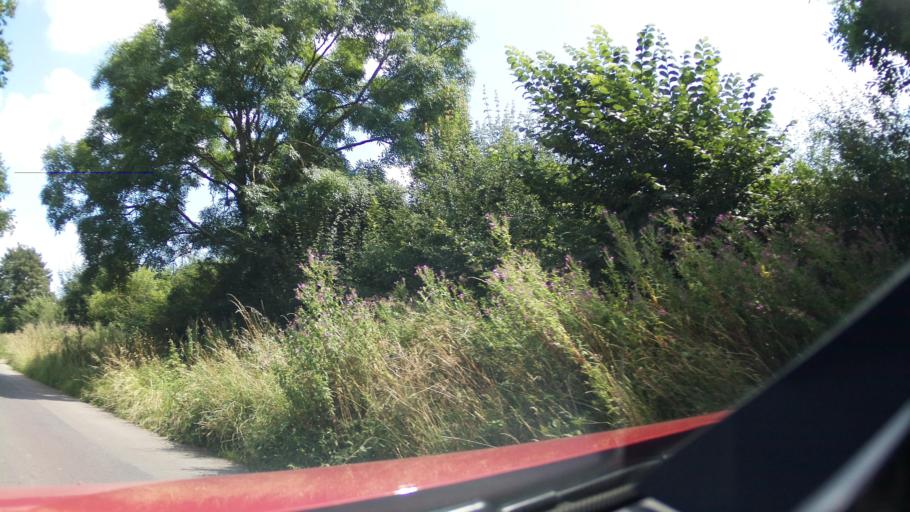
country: GB
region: England
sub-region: Wiltshire
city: Hankerton
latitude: 51.6086
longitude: -2.0492
